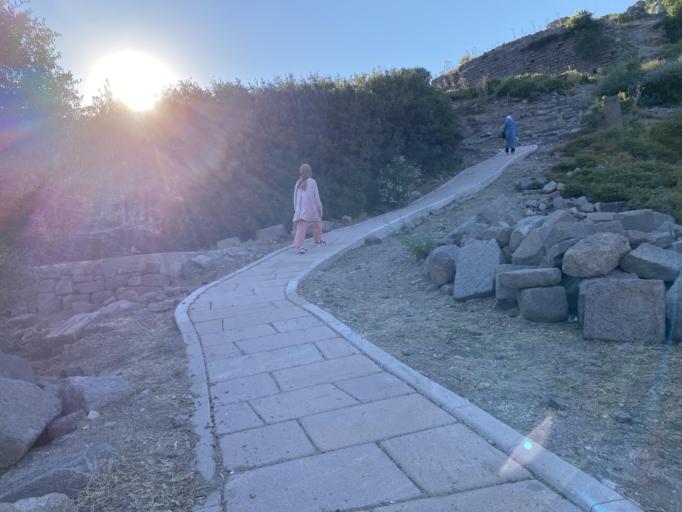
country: TR
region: Canakkale
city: Behram
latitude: 39.4878
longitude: 26.3374
